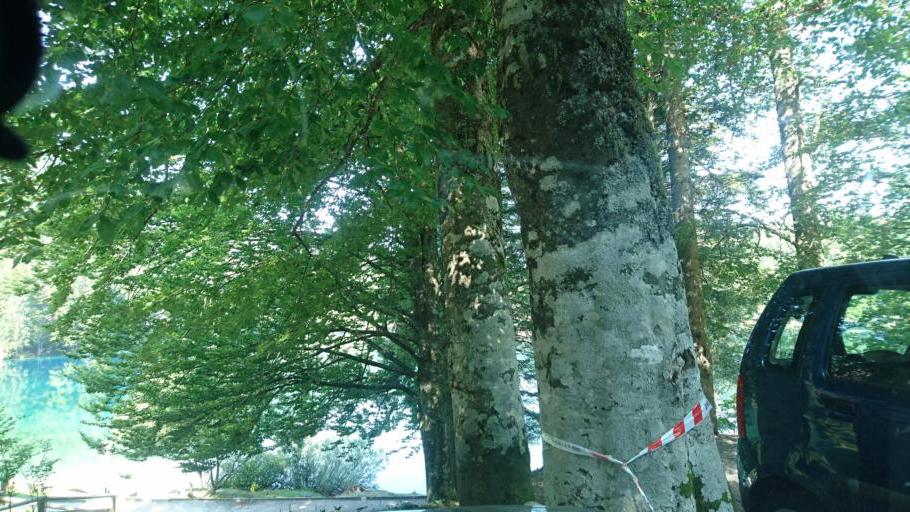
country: AT
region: Carinthia
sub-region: Politischer Bezirk Villach Land
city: Arnoldstein
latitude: 46.4805
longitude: 13.6735
